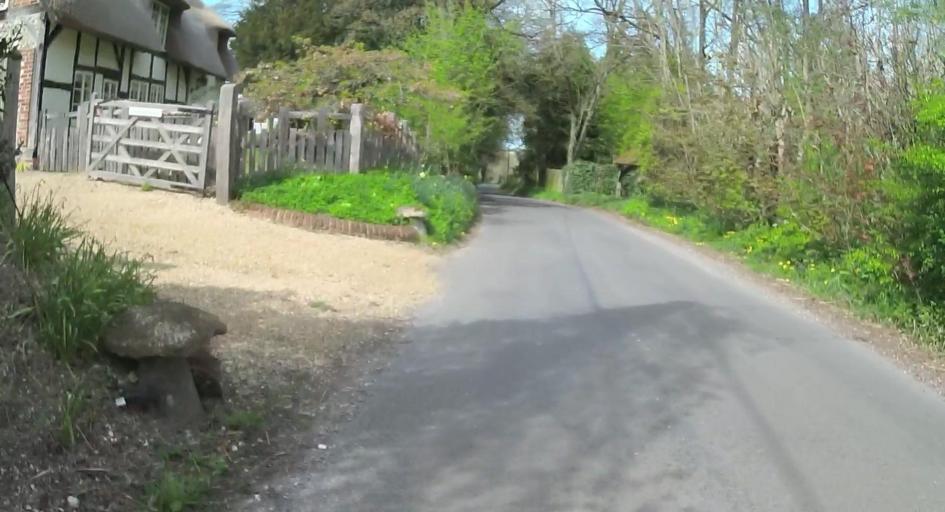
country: GB
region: England
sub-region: Hampshire
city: Chandlers Ford
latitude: 51.0778
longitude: -1.4553
